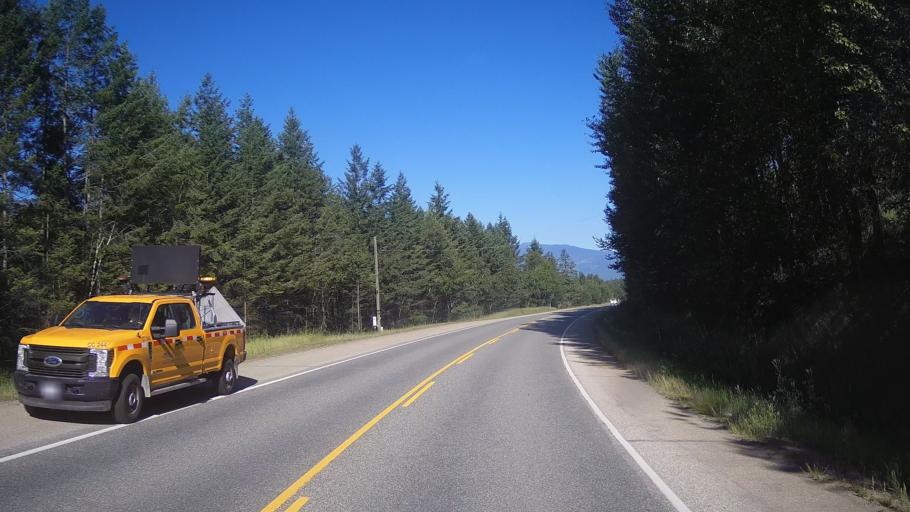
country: CA
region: British Columbia
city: Chase
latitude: 51.5943
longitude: -119.8740
